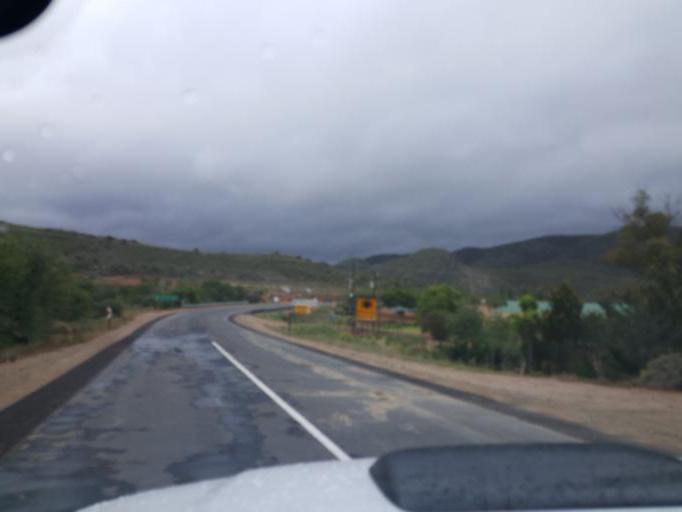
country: ZA
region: Western Cape
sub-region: Eden District Municipality
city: Oudtshoorn
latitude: -33.4049
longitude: 22.2189
